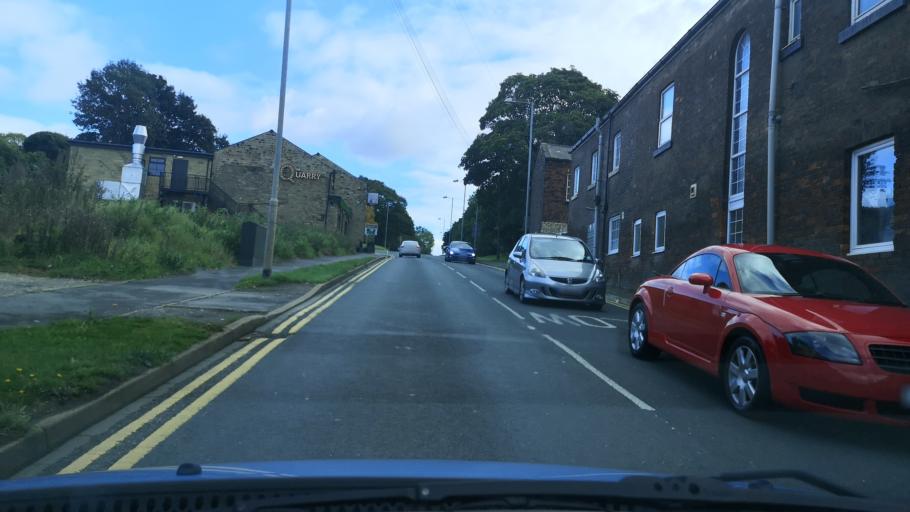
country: GB
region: England
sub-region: City and Borough of Wakefield
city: Horbury
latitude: 53.6587
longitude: -1.5655
